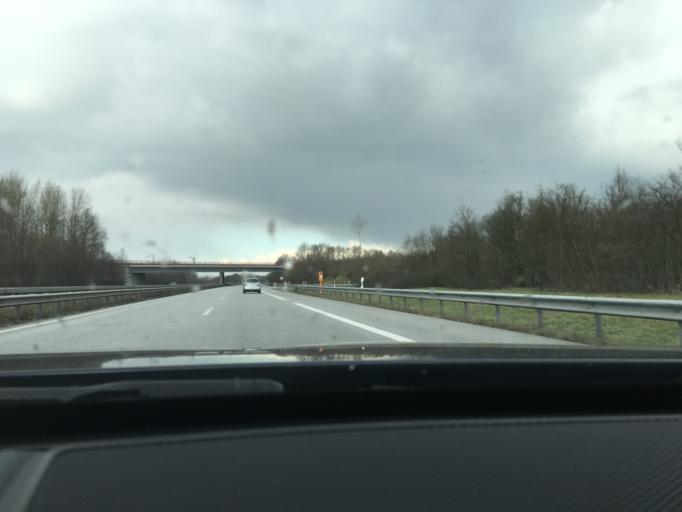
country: DE
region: Lower Saxony
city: Driftsethe
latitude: 53.4400
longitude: 8.5827
